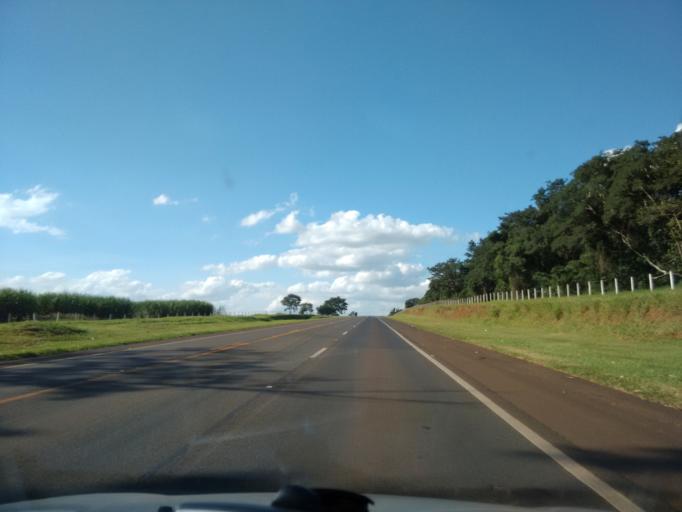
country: BR
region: Sao Paulo
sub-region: Americo Brasiliense
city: Americo Brasiliense
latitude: -21.7011
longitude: -48.0244
